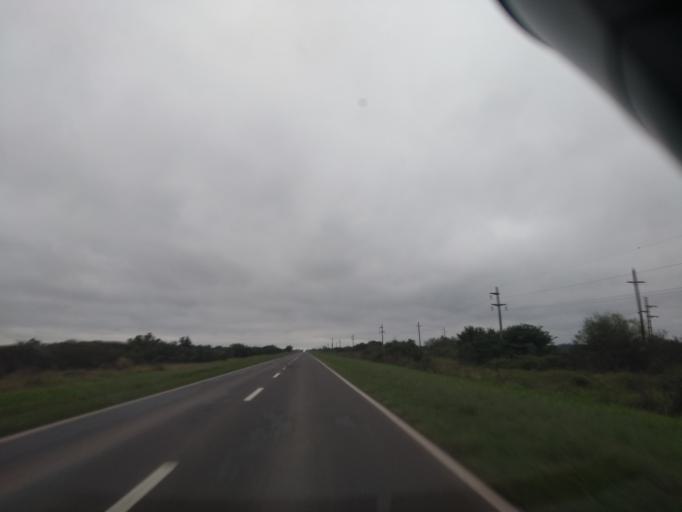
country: AR
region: Chaco
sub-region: Departamento de Quitilipi
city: Quitilipi
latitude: -26.8603
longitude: -60.2835
